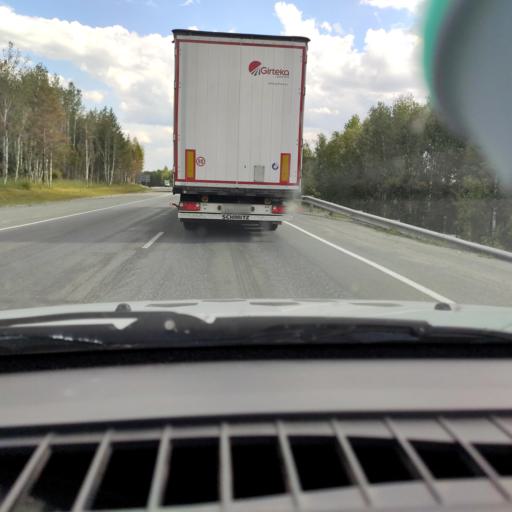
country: RU
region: Chelyabinsk
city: Zlatoust
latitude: 55.0252
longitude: 59.7242
